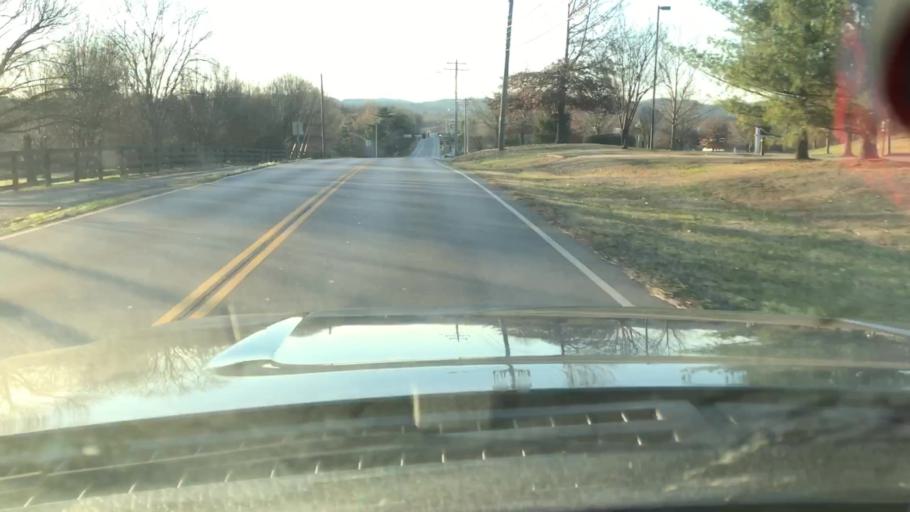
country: US
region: Tennessee
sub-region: Williamson County
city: Brentwood Estates
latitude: 35.9768
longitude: -86.7687
